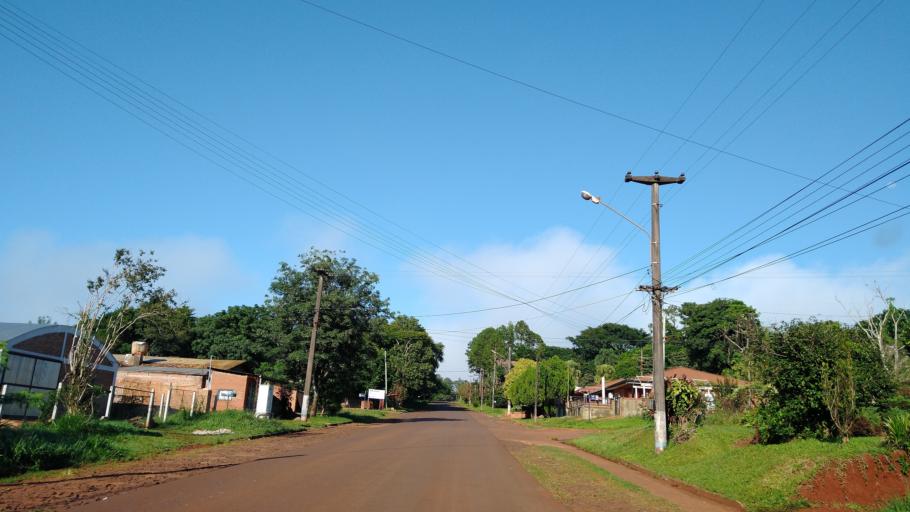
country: AR
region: Misiones
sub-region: Departamento de Montecarlo
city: Montecarlo
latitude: -26.5618
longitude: -54.7819
